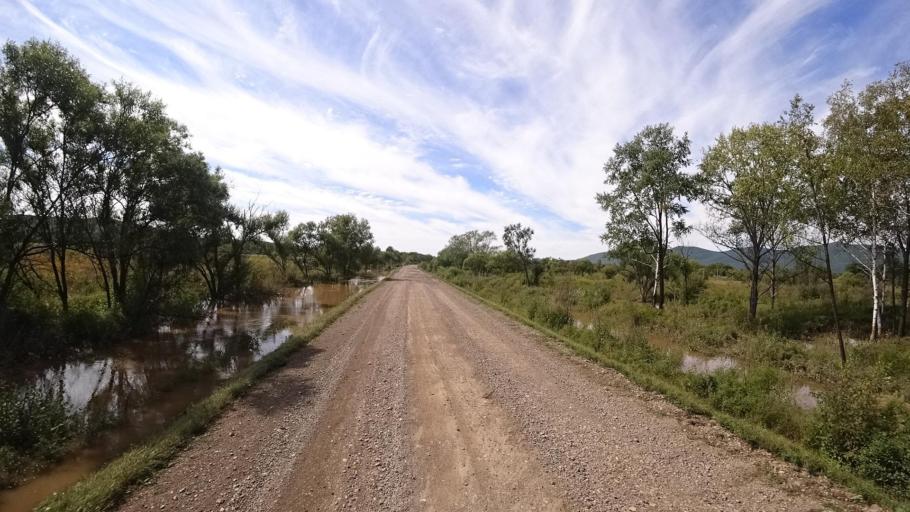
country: RU
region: Primorskiy
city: Kirovskiy
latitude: 44.7695
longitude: 133.6225
